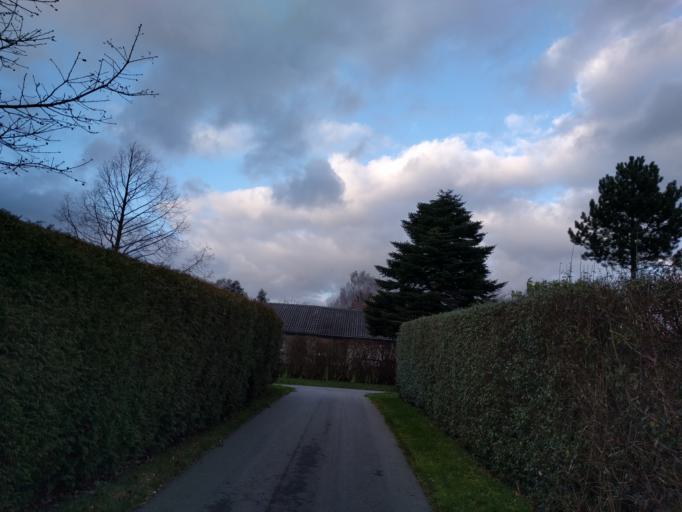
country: DK
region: Central Jutland
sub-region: Silkeborg Kommune
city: Silkeborg
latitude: 56.1896
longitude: 9.5194
